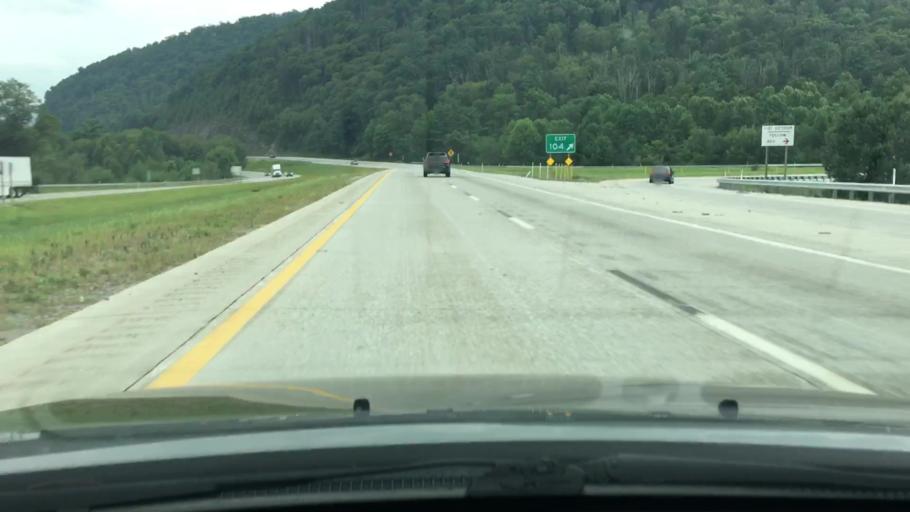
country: US
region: Pennsylvania
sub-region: Schuylkill County
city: Tremont
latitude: 40.5916
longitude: -76.4126
